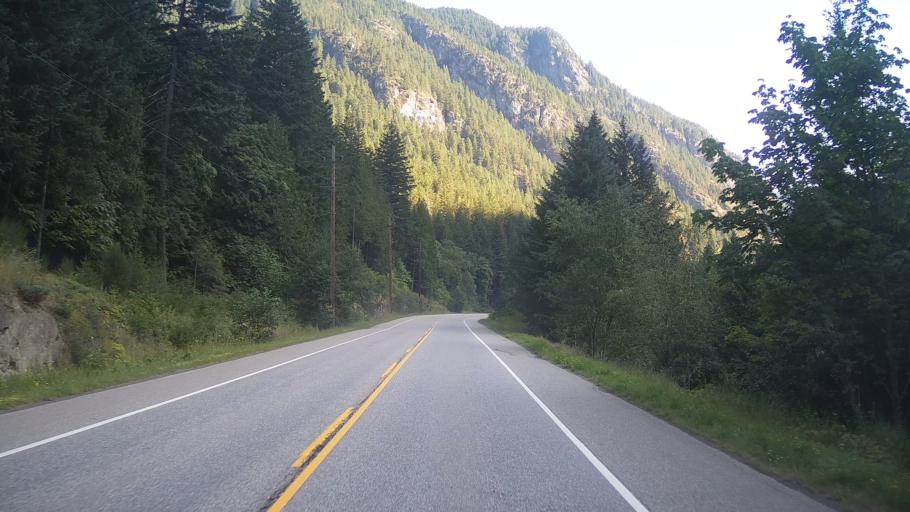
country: CA
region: British Columbia
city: Hope
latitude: 49.6075
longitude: -121.4154
